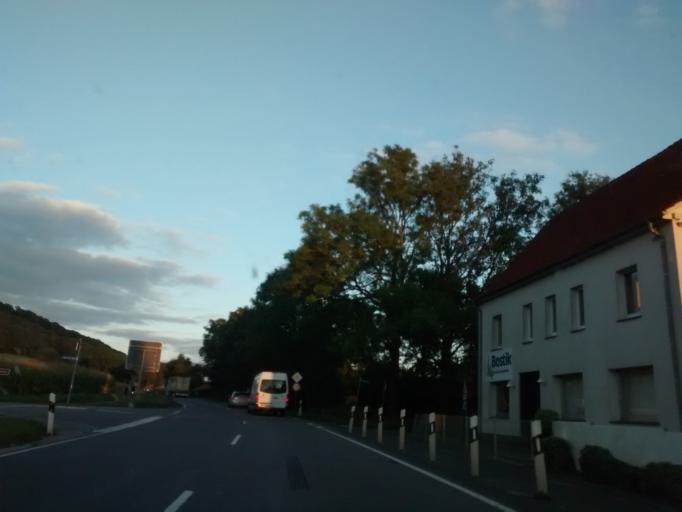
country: DE
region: North Rhine-Westphalia
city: Borgholzhausen
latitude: 52.0822
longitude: 8.2841
